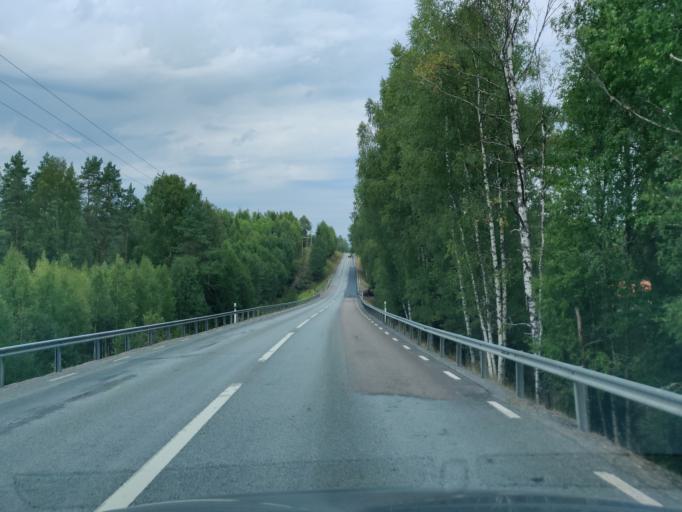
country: SE
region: Vaermland
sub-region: Munkfors Kommun
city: Munkfors
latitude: 59.9201
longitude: 13.5723
